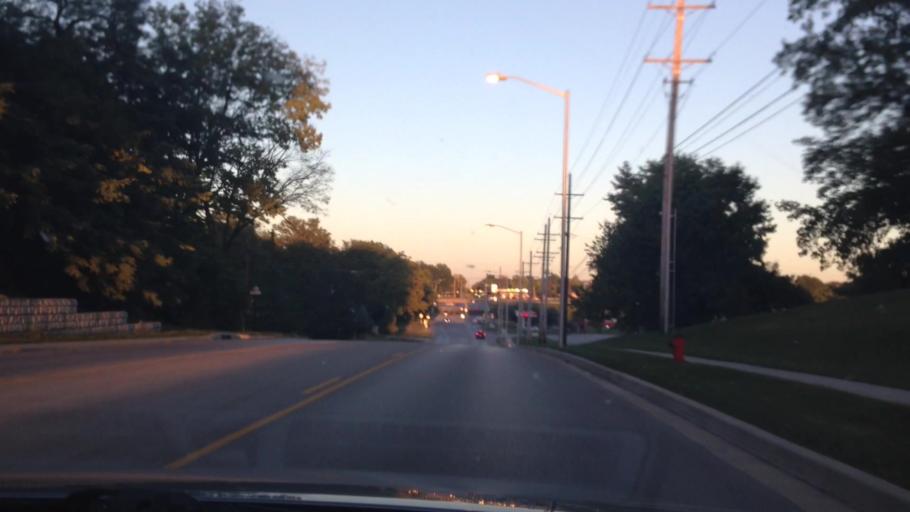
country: US
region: Missouri
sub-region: Platte County
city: Parkville
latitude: 39.2251
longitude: -94.6565
